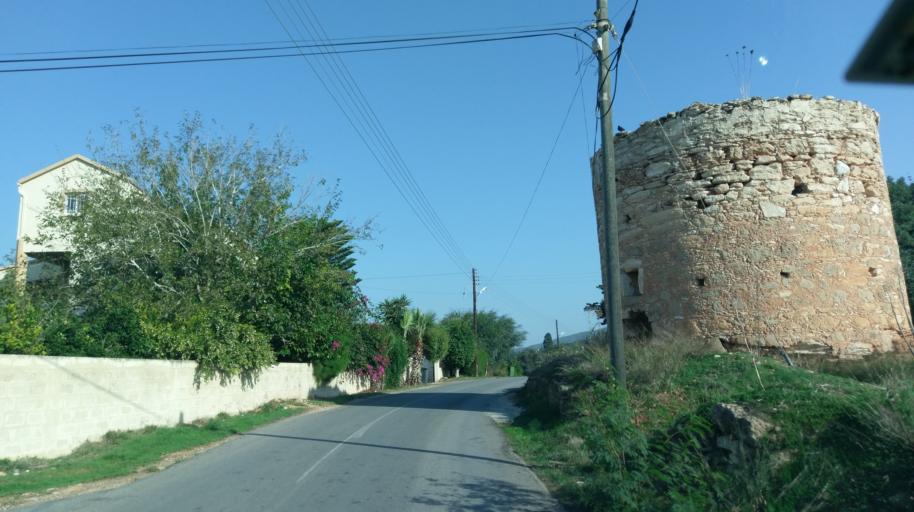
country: CY
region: Ammochostos
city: Leonarisso
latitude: 35.5356
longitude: 34.1979
